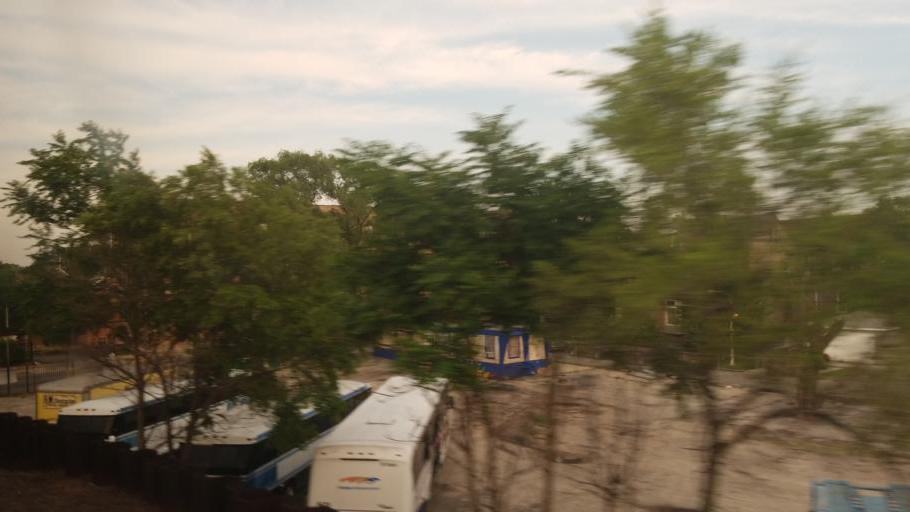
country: US
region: Illinois
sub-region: Cook County
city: Chicago
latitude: 41.8550
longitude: -87.6964
